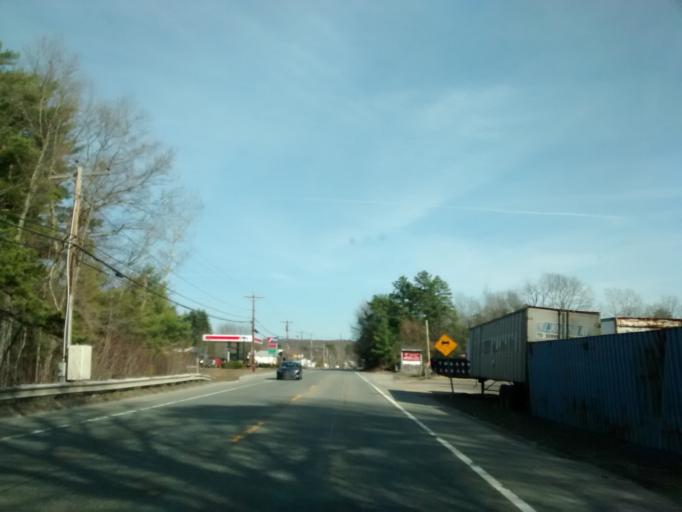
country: US
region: Massachusetts
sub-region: Worcester County
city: Millville
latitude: 42.0317
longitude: -71.6134
